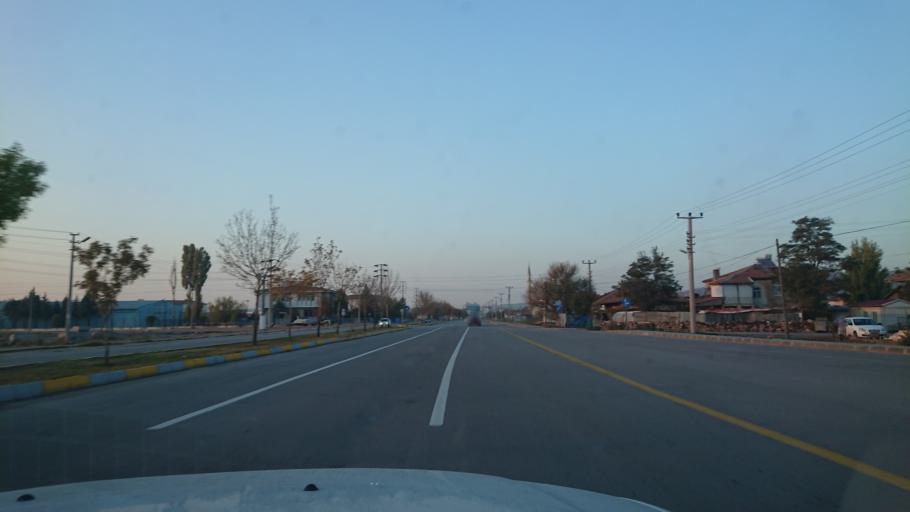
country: TR
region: Aksaray
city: Aksaray
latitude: 38.3443
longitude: 34.0455
